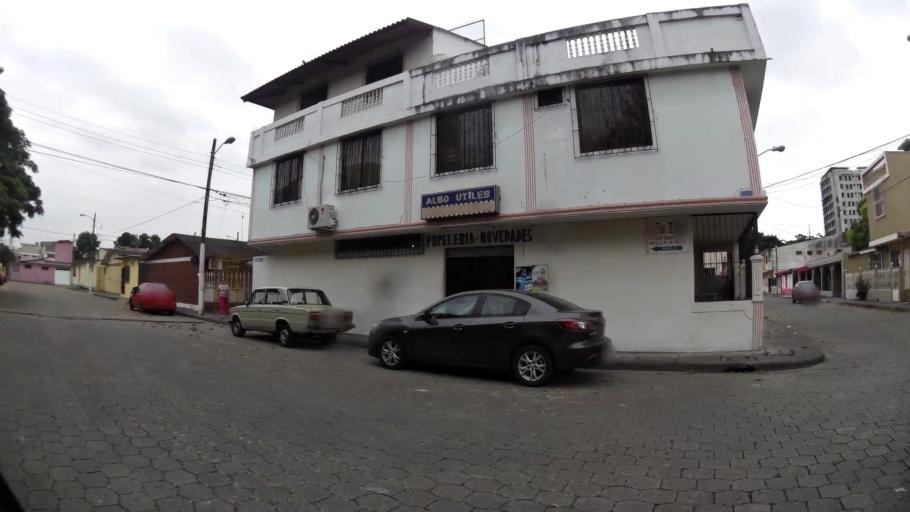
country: EC
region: Guayas
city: Eloy Alfaro
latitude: -2.1375
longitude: -79.9030
